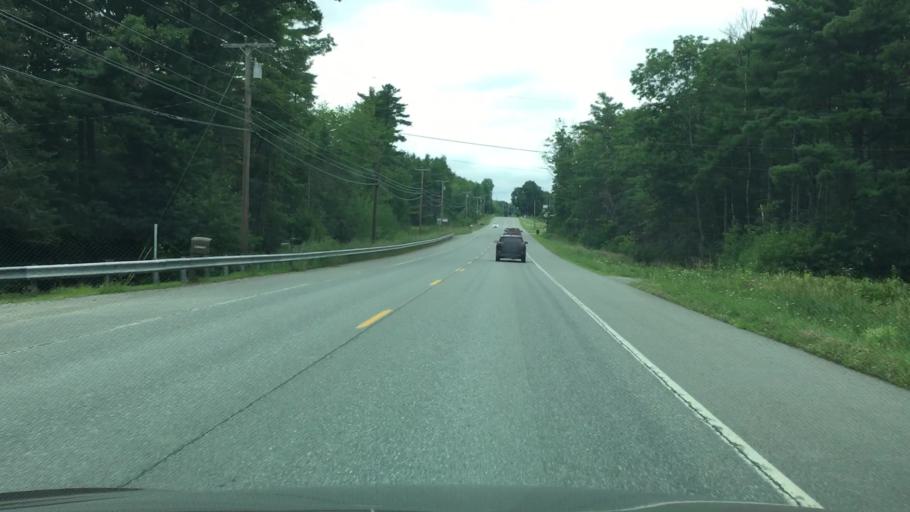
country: US
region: Maine
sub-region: Penobscot County
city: Orrington
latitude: 44.7075
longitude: -68.8241
